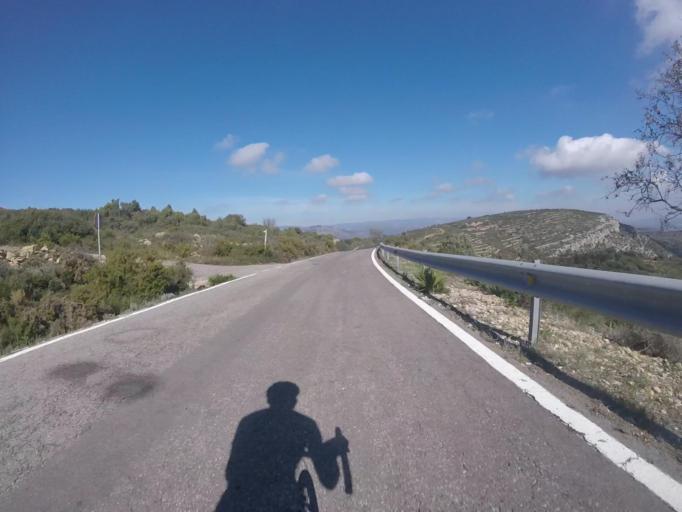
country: ES
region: Valencia
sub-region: Provincia de Castello
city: Albocasser
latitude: 40.3419
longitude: 0.0496
